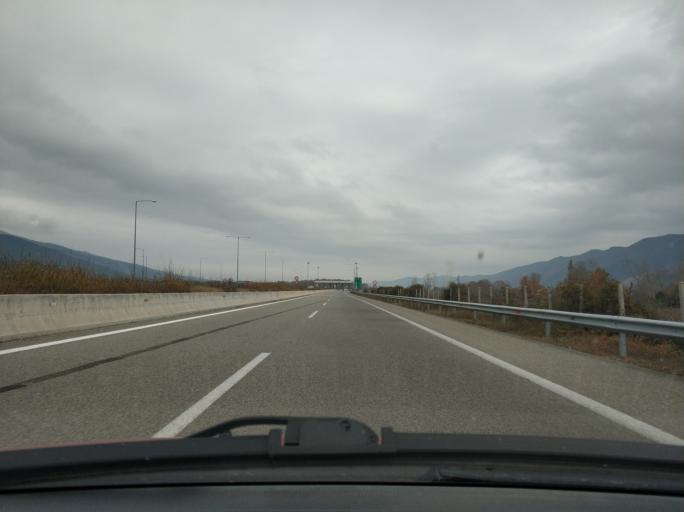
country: GR
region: East Macedonia and Thrace
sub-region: Nomos Kavalas
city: Palaiochori
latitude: 40.8562
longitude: 24.1581
